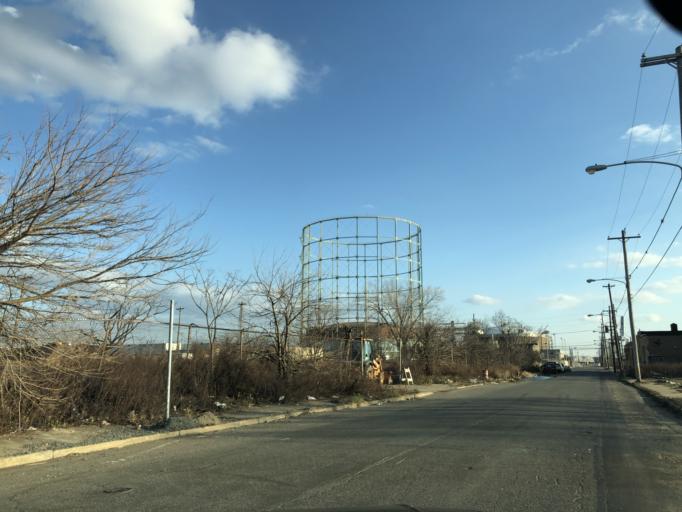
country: US
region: New Jersey
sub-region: Camden County
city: Pennsauken
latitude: 39.9861
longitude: -75.0907
